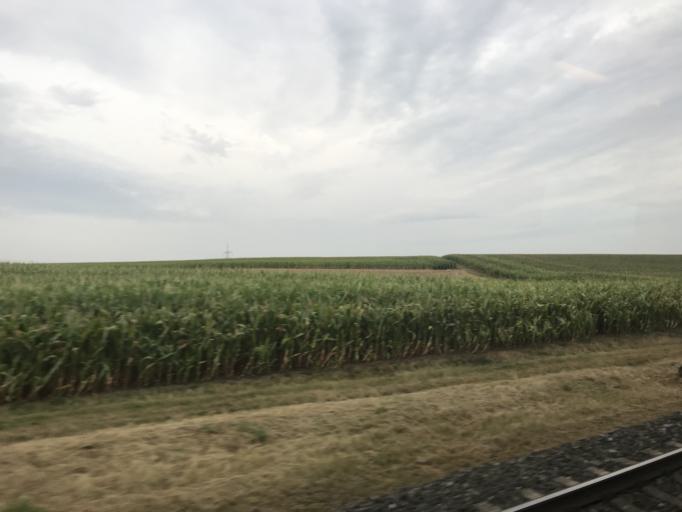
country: DE
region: Bavaria
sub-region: Regierungsbezirk Unterfranken
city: Waigolshausen
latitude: 49.9764
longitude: 10.1480
